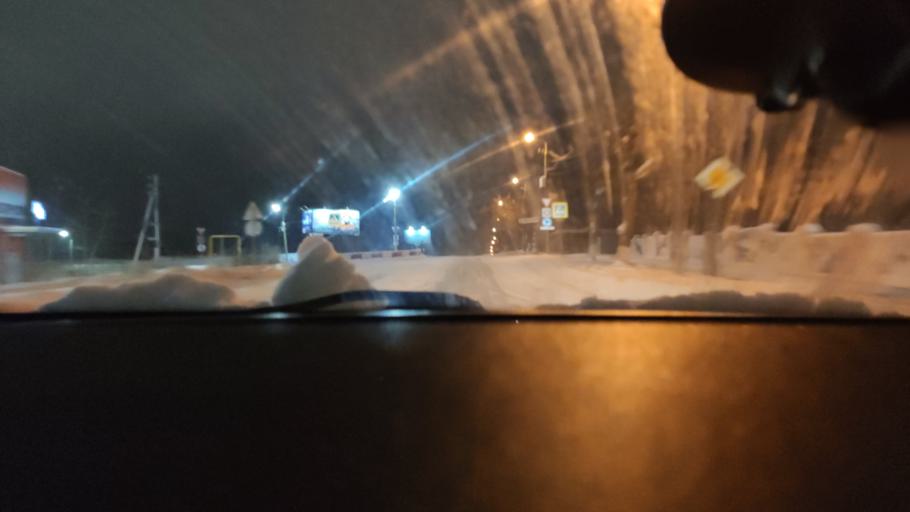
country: RU
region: Perm
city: Krasnokamsk
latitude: 58.0818
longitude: 55.7700
